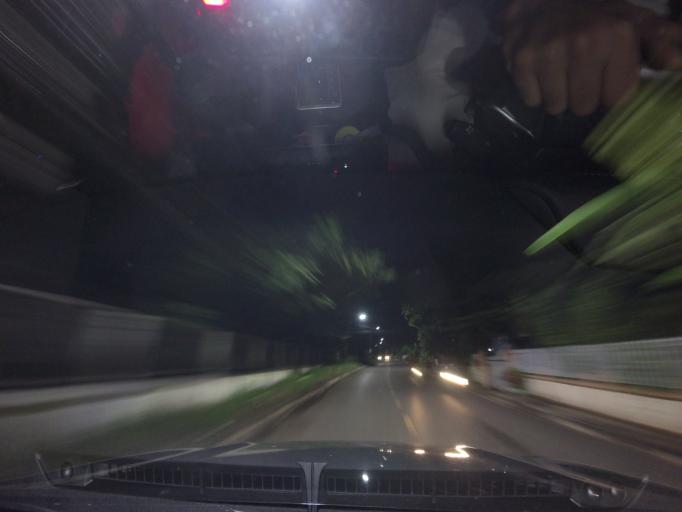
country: TH
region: Nong Khai
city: Nong Khai
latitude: 17.8726
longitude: 102.7159
